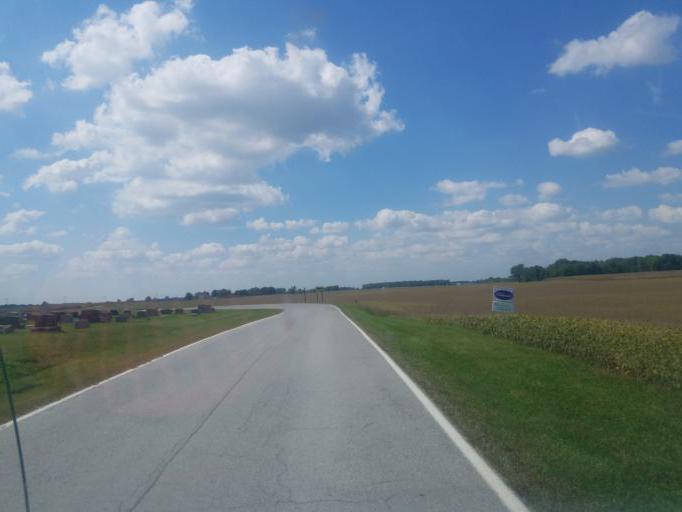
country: US
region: Ohio
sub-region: Hardin County
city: Ada
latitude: 40.6539
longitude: -83.8983
